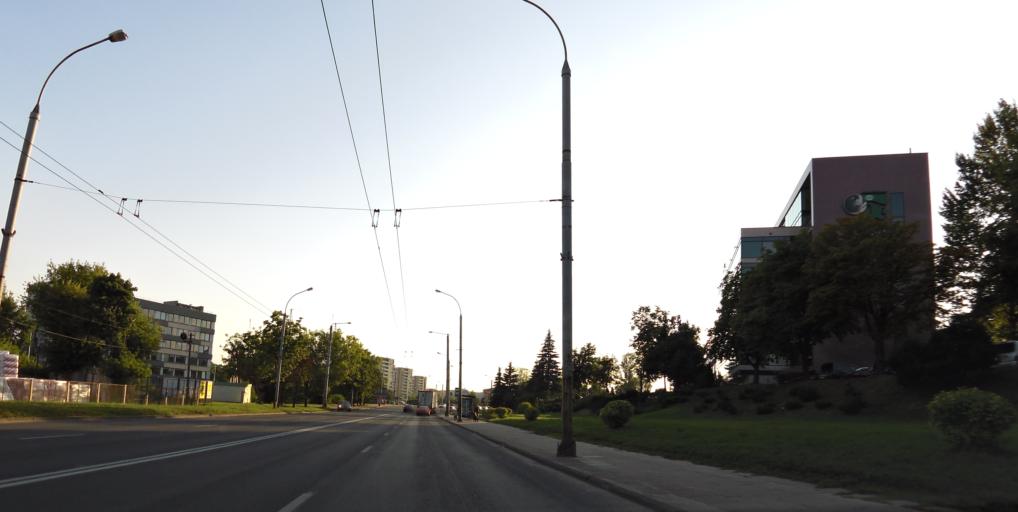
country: LT
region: Vilnius County
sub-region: Vilnius
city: Vilnius
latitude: 54.7158
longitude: 25.2902
